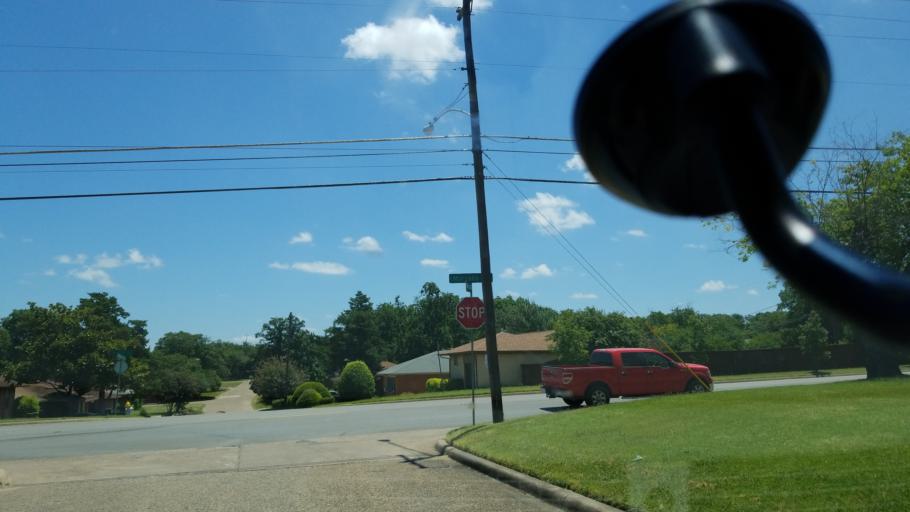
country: US
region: Texas
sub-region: Dallas County
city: Cockrell Hill
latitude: 32.6814
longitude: -96.8149
